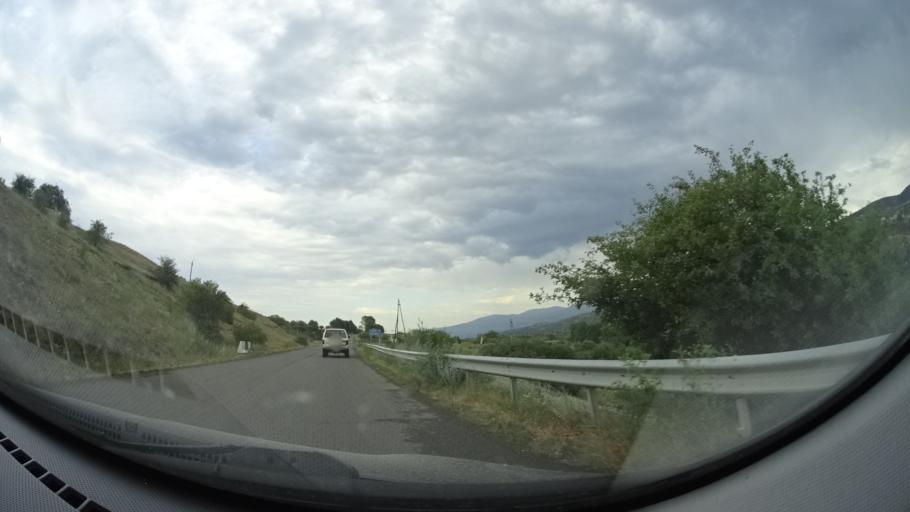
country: GE
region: Samtskhe-Javakheti
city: Adigeni
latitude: 41.6644
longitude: 42.7462
